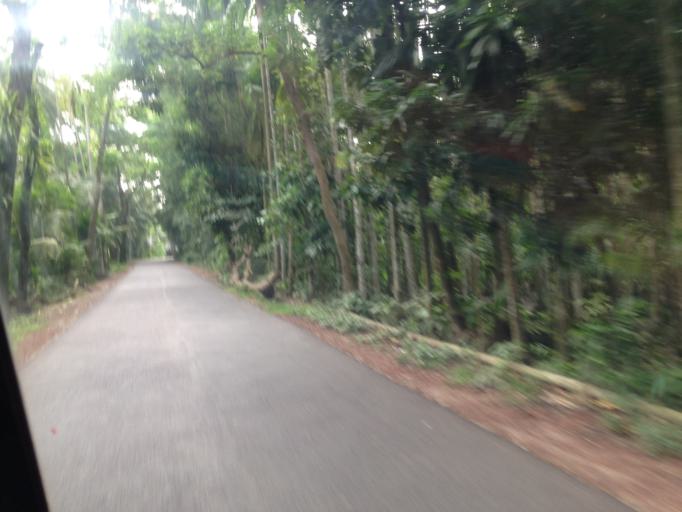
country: BD
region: Chittagong
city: Raipur
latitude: 23.0351
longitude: 90.7458
